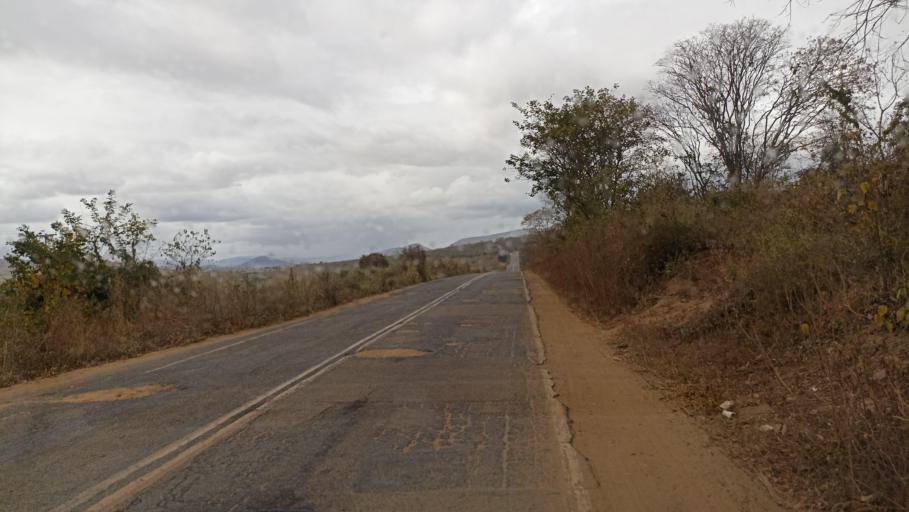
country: BR
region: Minas Gerais
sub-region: Itinga
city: Itinga
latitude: -16.6376
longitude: -41.8093
